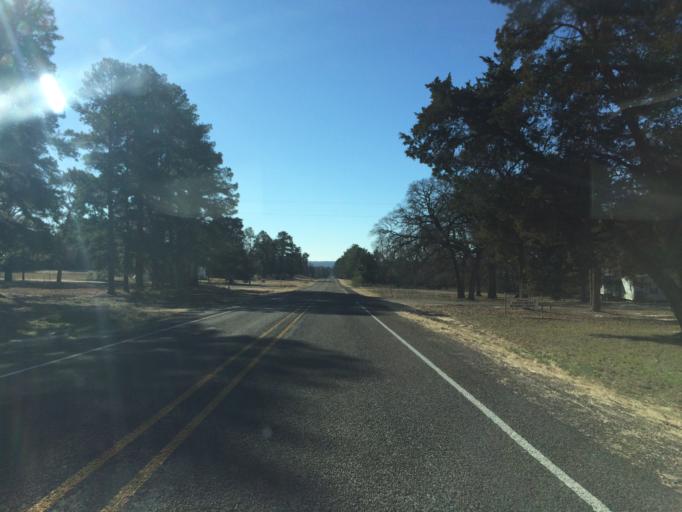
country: US
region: Texas
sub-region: Wood County
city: Hawkins
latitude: 32.6288
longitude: -95.2743
